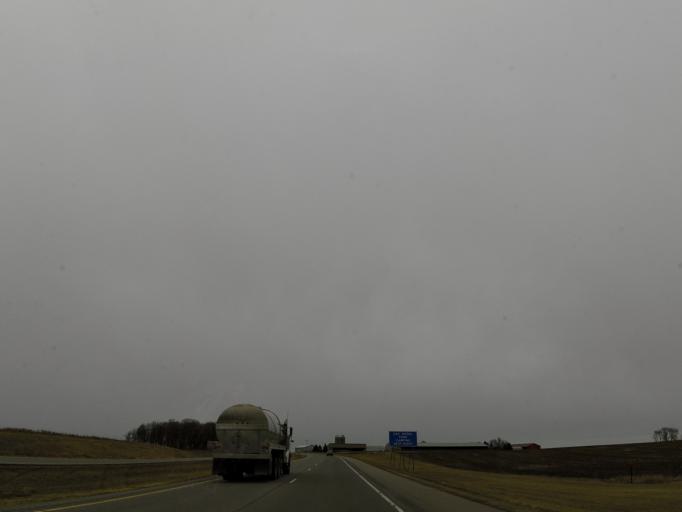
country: US
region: Minnesota
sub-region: Le Sueur County
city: Le Sueur
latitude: 44.5326
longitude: -93.8468
